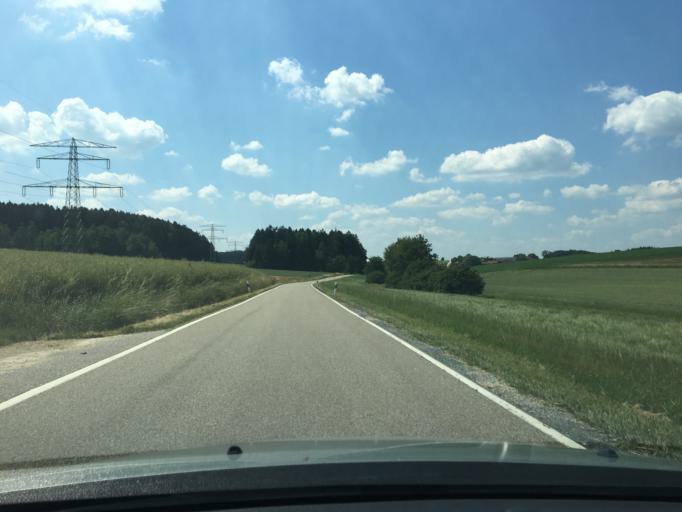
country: DE
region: Bavaria
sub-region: Upper Bavaria
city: Egglkofen
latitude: 48.4165
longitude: 12.4804
